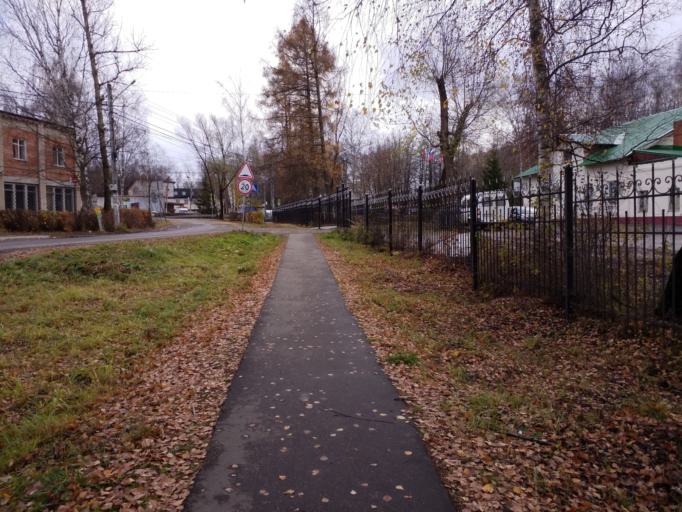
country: RU
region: Moskovskaya
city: Ashukino
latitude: 56.1625
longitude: 37.9439
